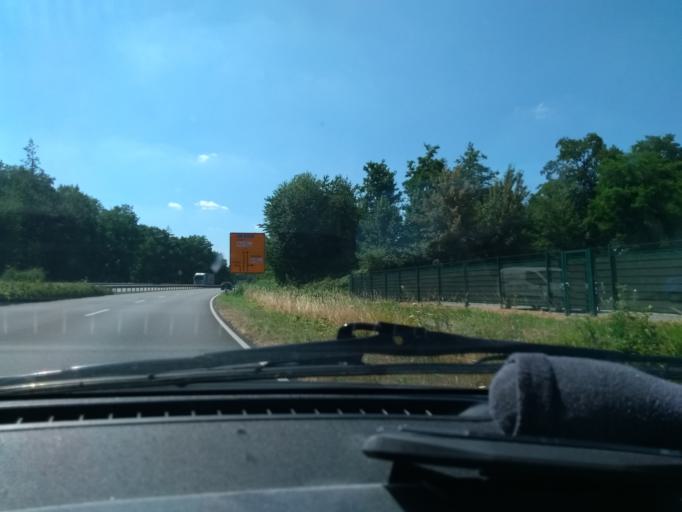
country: DE
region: Lower Saxony
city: Meppen
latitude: 52.6786
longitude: 7.3036
